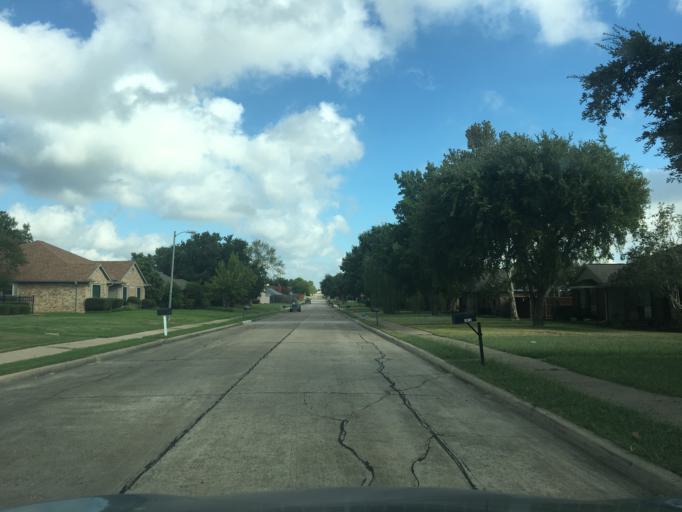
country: US
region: Texas
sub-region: Dallas County
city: Sachse
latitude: 32.9675
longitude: -96.5886
